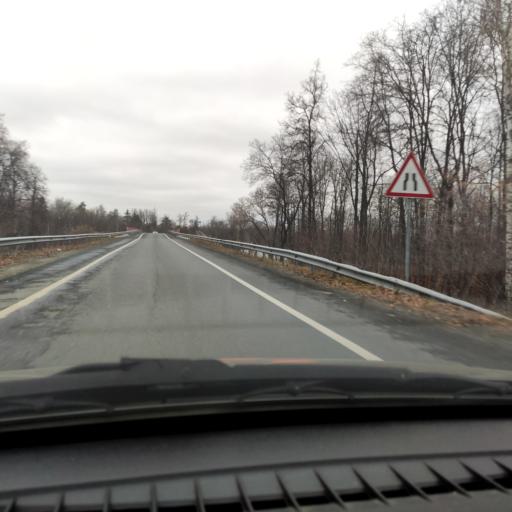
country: RU
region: Samara
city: Pribrezhnyy
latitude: 53.5108
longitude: 49.9306
